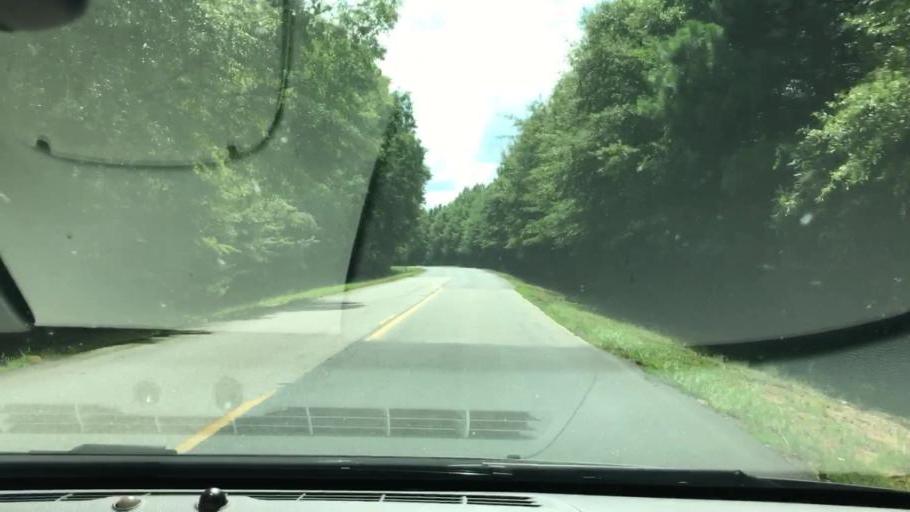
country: US
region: Georgia
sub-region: Quitman County
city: Georgetown
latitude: 31.9874
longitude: -85.0485
